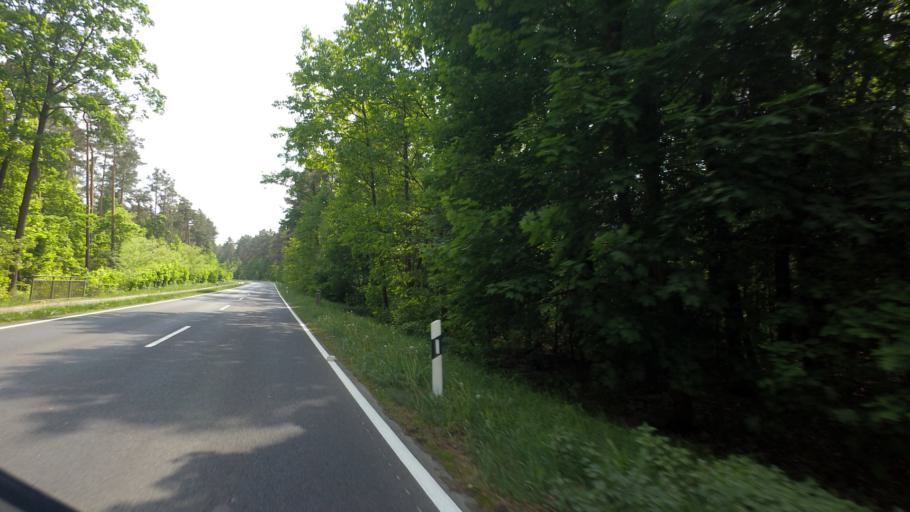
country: DE
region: Saxony
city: Niesky
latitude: 51.3102
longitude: 14.8258
